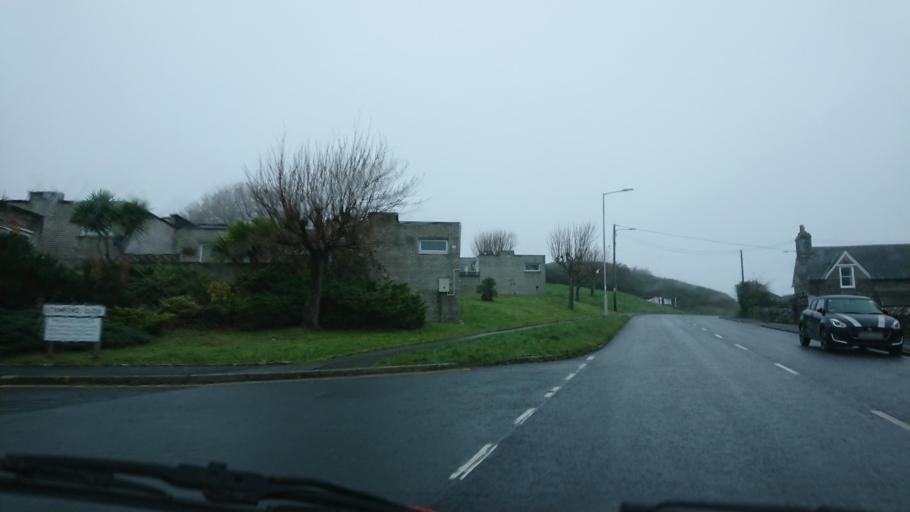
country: GB
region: England
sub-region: Plymouth
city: Plymstock
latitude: 50.3545
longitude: -4.1170
